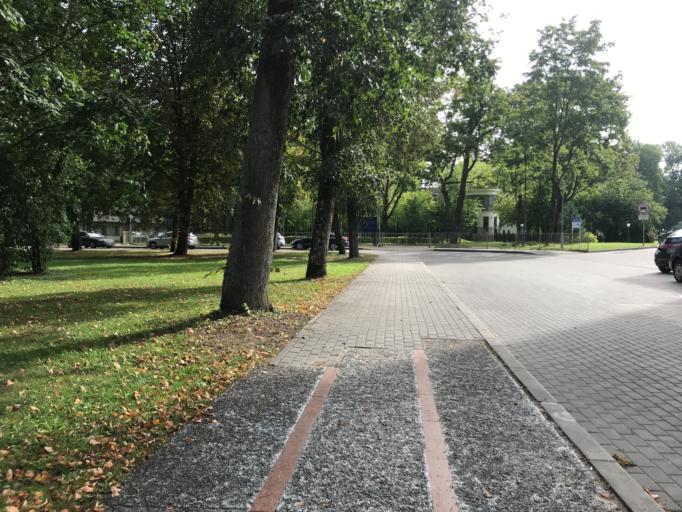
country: LT
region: Alytaus apskritis
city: Druskininkai
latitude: 54.0197
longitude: 23.9766
